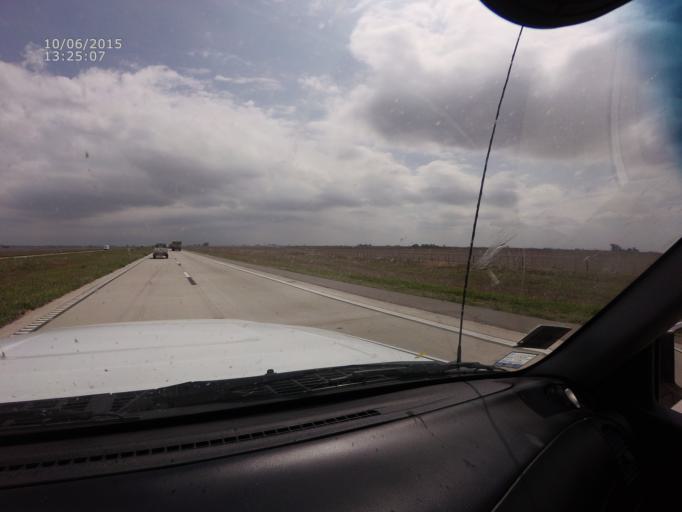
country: AR
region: Cordoba
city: Marcos Juarez
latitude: -32.6541
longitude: -62.1535
